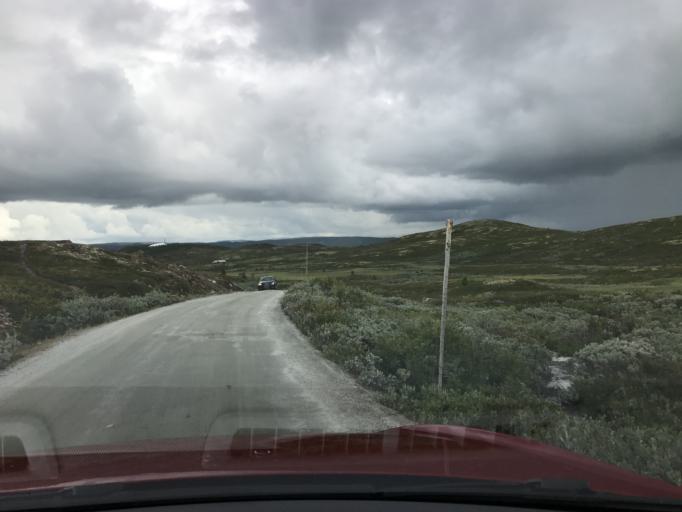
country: NO
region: Buskerud
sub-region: Hol
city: Geilo
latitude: 60.5463
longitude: 8.1616
